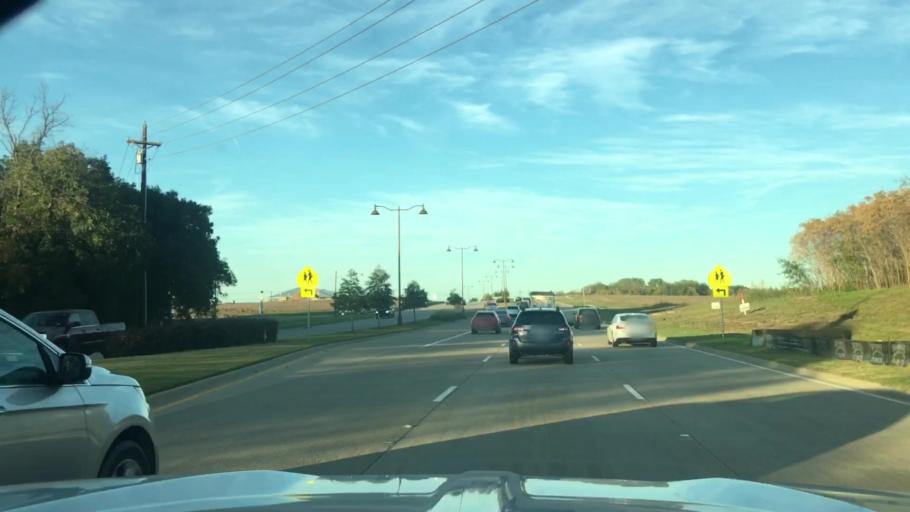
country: US
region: Texas
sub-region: Collin County
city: Prosper
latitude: 33.2290
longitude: -96.7939
